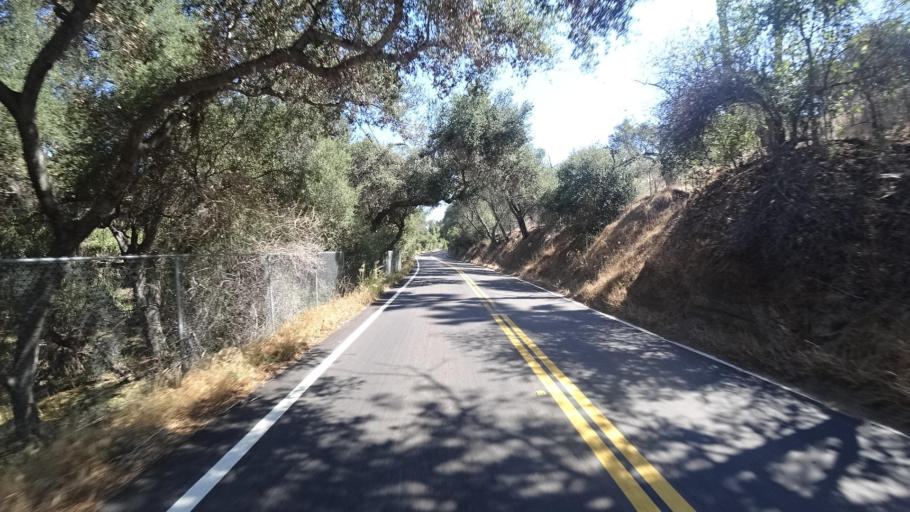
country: US
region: California
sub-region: San Diego County
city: Fallbrook
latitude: 33.3434
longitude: -117.2243
